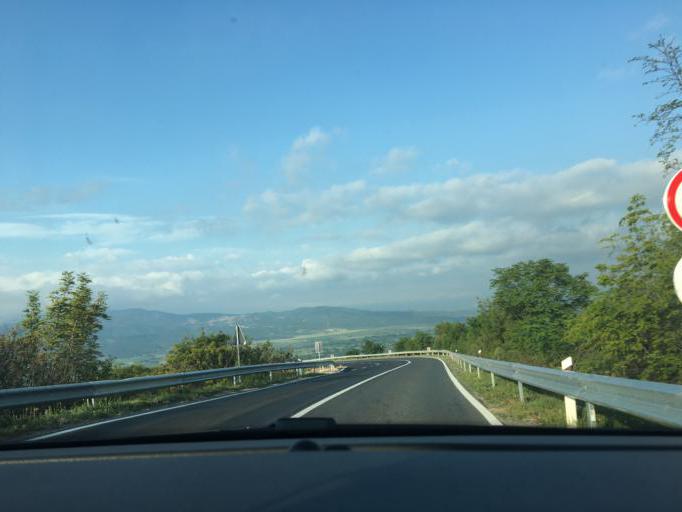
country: MK
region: Valandovo
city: Valandovo
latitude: 41.3256
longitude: 22.5971
